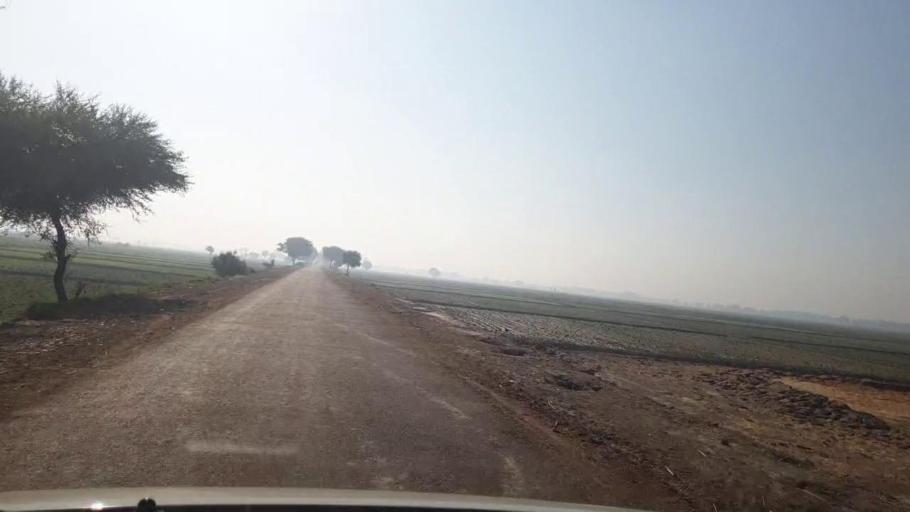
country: PK
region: Sindh
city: Dadu
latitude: 26.6703
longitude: 67.8148
